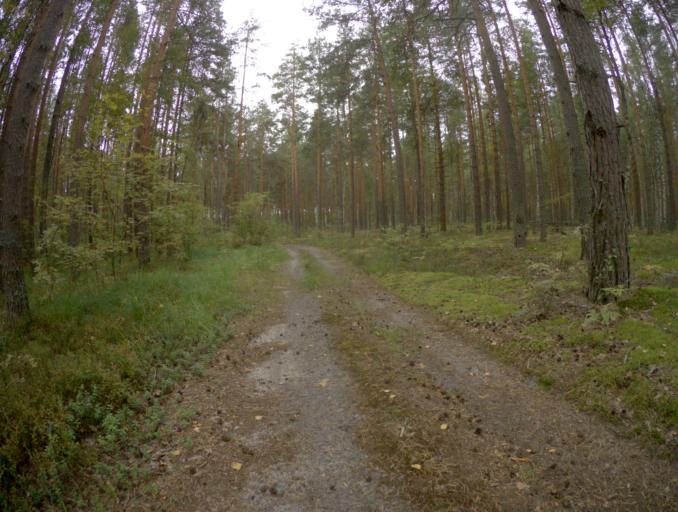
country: RU
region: Vladimir
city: Ivanishchi
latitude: 55.8292
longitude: 40.3019
